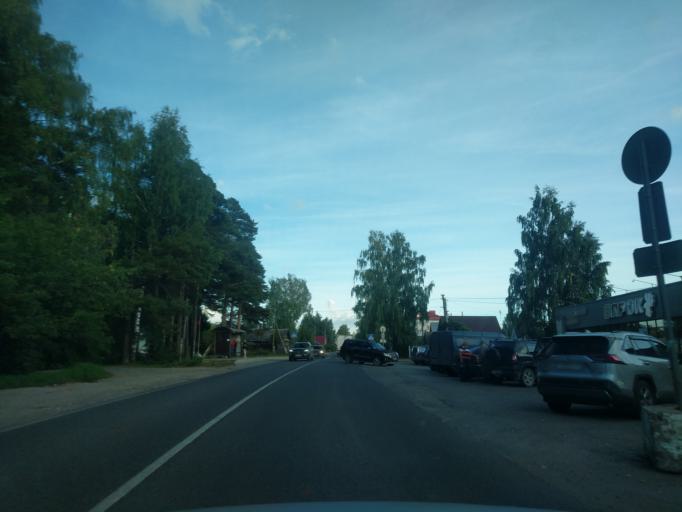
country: RU
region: Kirov
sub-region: Kirovo-Chepetskiy Rayon
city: Kirov
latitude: 58.6102
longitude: 49.7985
